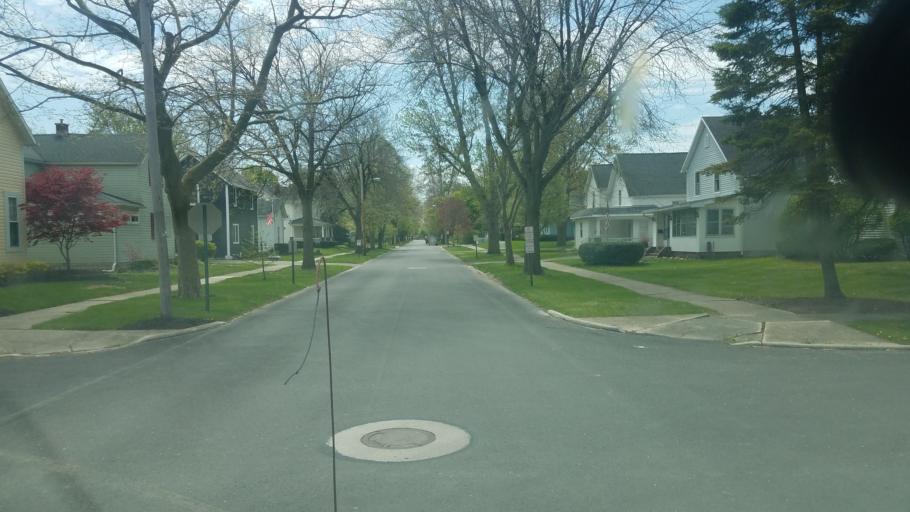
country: US
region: Ohio
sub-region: Hardin County
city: Ada
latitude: 40.7654
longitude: -83.8216
